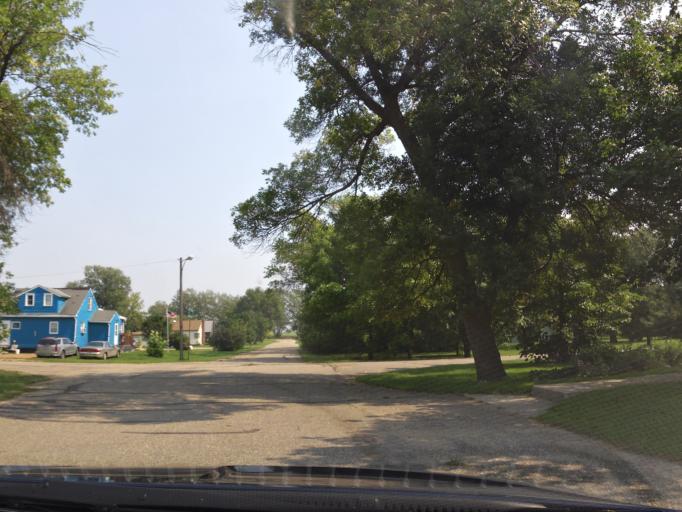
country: US
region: South Dakota
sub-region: Roberts County
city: Sisseton
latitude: 45.8569
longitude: -97.1007
